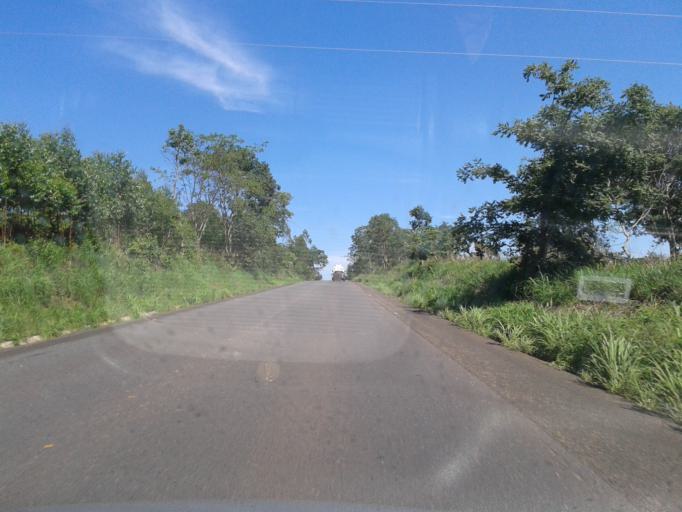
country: BR
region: Goias
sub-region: Bela Vista De Goias
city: Bela Vista de Goias
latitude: -17.1248
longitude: -48.8369
